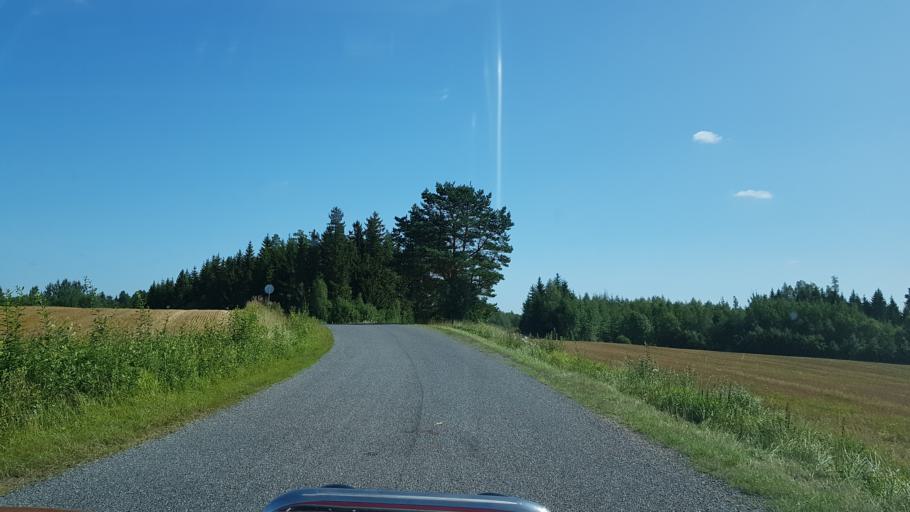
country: EE
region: Vorumaa
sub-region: Voru linn
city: Voru
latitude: 57.7543
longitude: 27.2896
